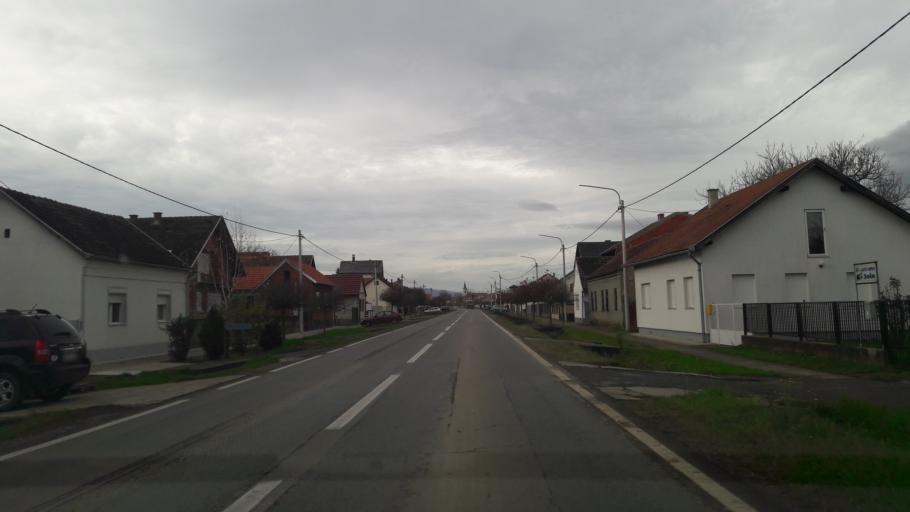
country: HR
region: Osjecko-Baranjska
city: Fericanci
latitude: 45.5238
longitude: 17.9883
